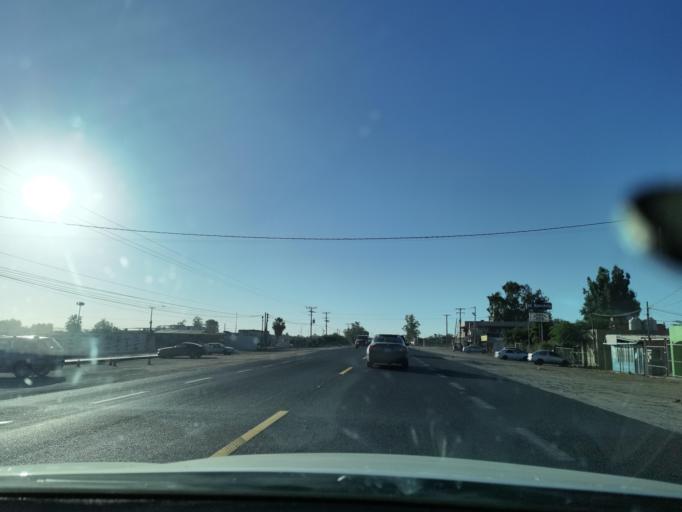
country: MX
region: Baja California
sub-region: Mexicali
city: Islas Agrarias Grupo A
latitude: 32.6475
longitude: -115.3283
